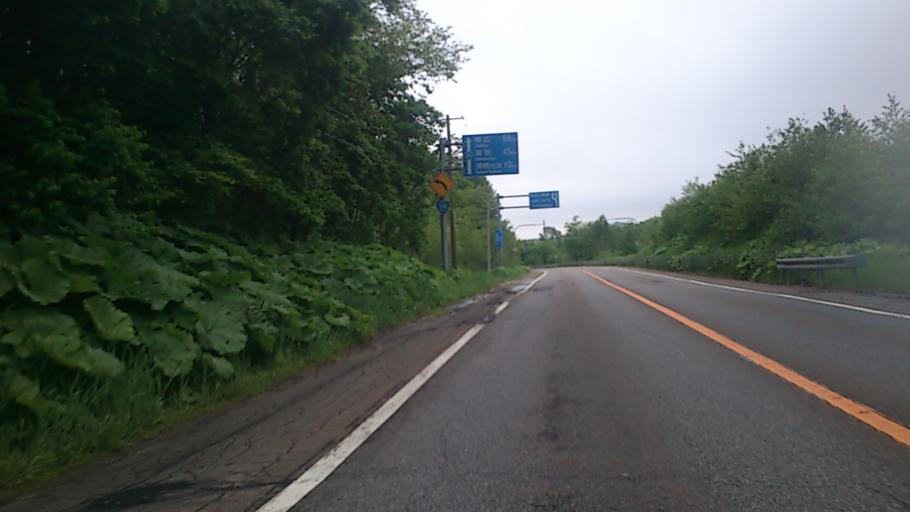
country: JP
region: Hokkaido
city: Obihiro
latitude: 42.8326
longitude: 143.7645
